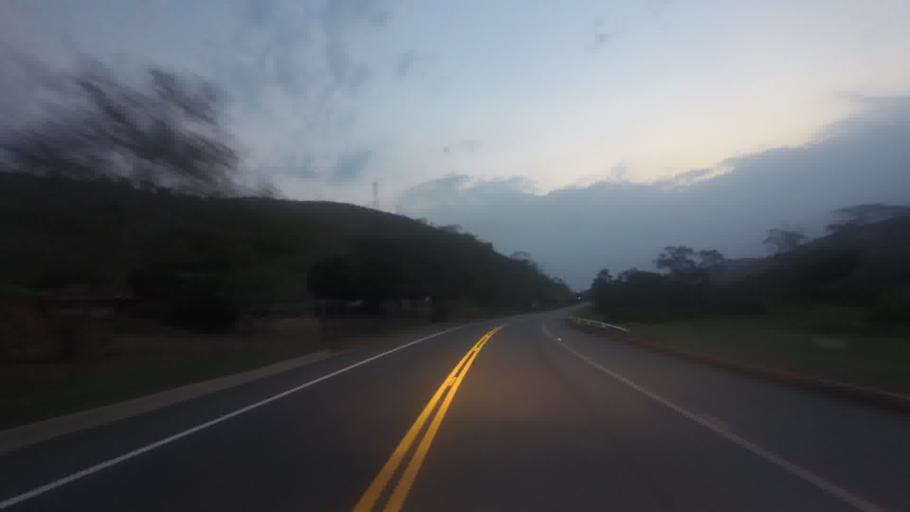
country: BR
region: Minas Gerais
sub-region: Alem Paraiba
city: Alem Paraiba
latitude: -21.9201
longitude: -42.7634
